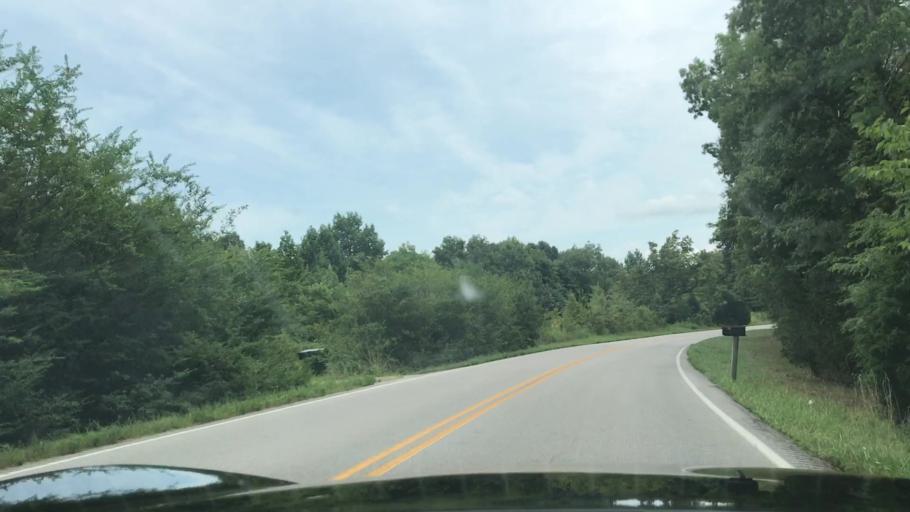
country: US
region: Kentucky
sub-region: Butler County
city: Morgantown
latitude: 37.1818
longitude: -86.8673
